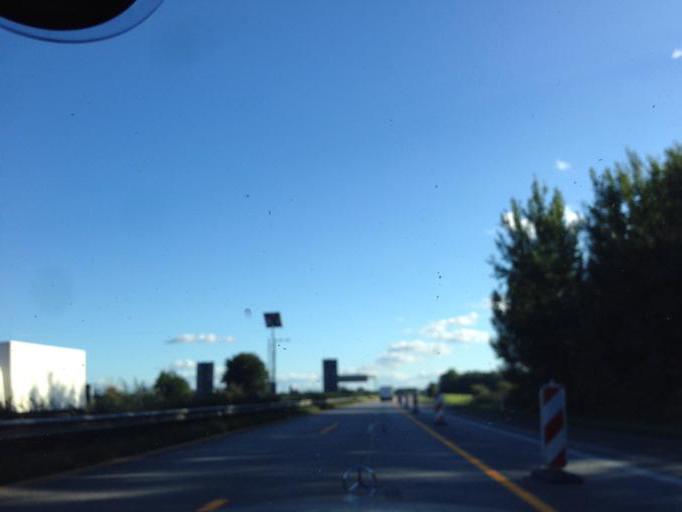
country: DE
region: Schleswig-Holstein
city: Schonbek
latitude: 54.1644
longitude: 9.9623
